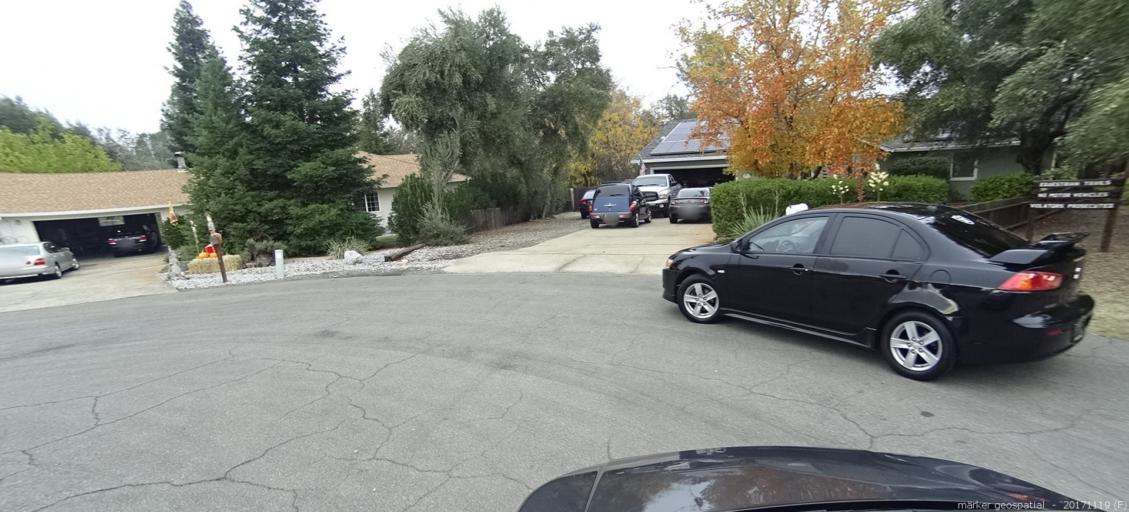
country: US
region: California
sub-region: Shasta County
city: Redding
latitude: 40.4892
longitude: -122.4140
